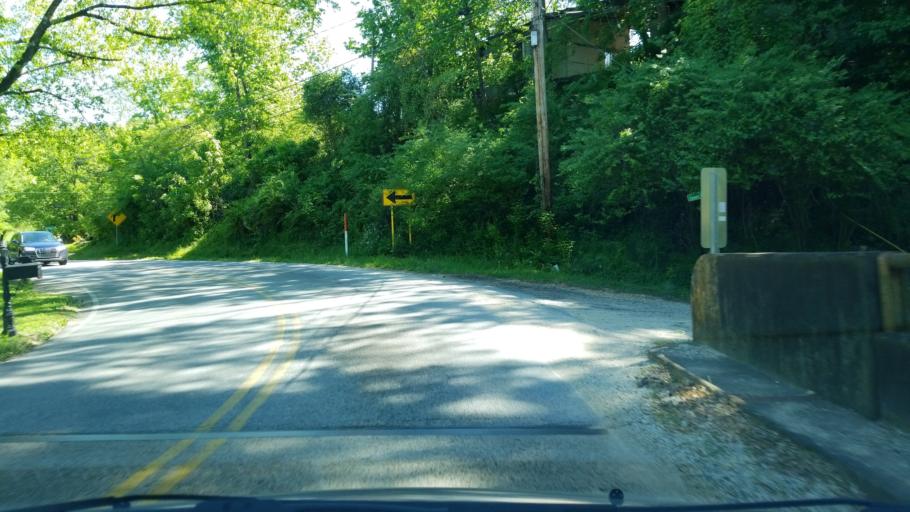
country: US
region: Tennessee
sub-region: Hamilton County
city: Falling Water
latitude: 35.1750
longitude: -85.2276
